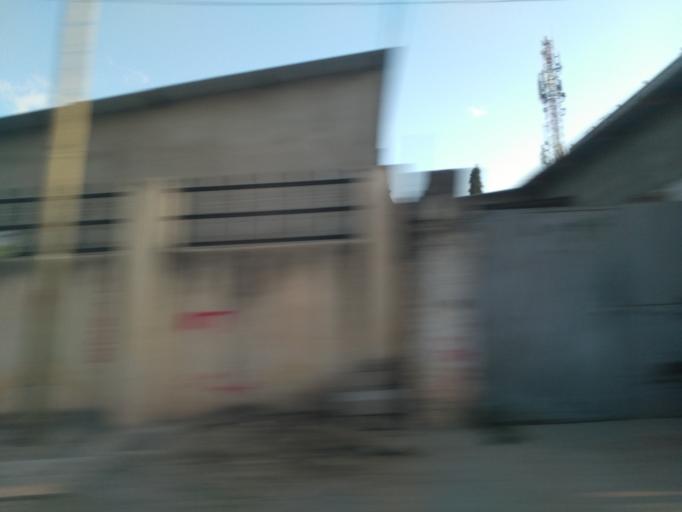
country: TZ
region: Dar es Salaam
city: Magomeni
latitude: -6.7619
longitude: 39.2667
